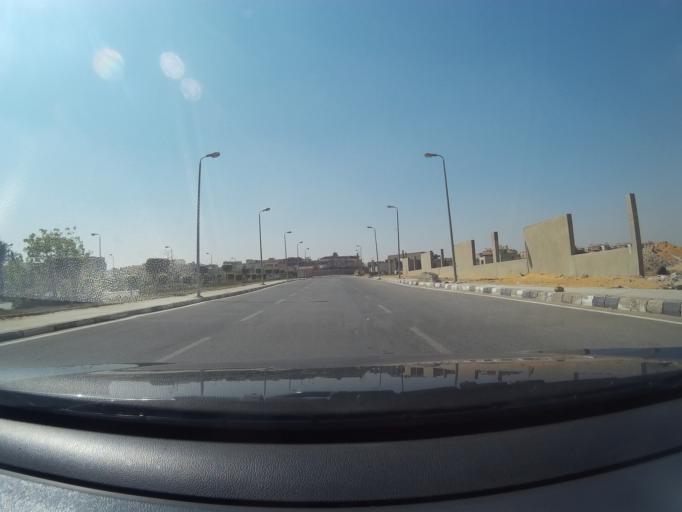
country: EG
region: Muhafazat al Qahirah
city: Cairo
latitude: 30.0151
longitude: 31.4095
